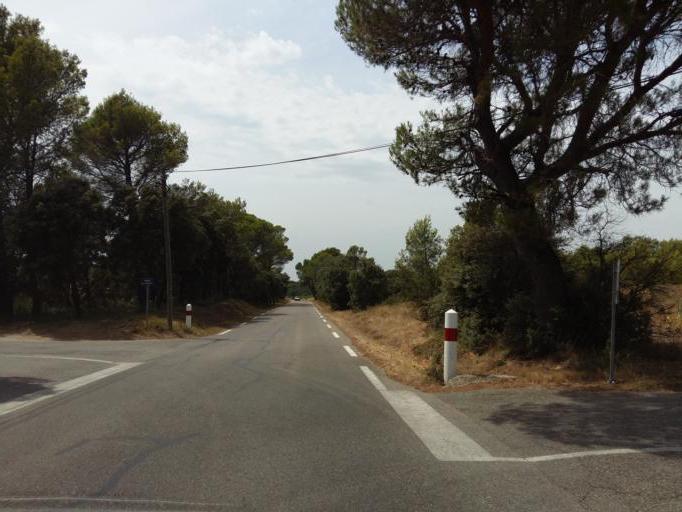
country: FR
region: Provence-Alpes-Cote d'Azur
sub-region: Departement du Vaucluse
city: Uchaux
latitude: 44.1992
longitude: 4.7952
